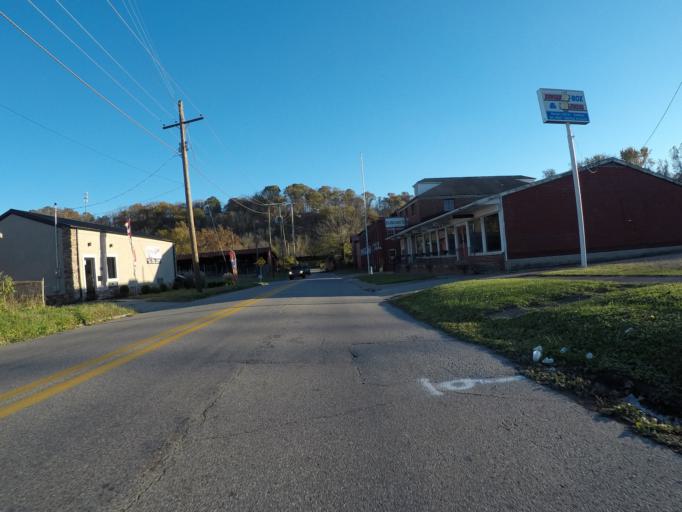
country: US
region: West Virginia
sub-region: Cabell County
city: Huntington
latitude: 38.4067
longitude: -82.4776
